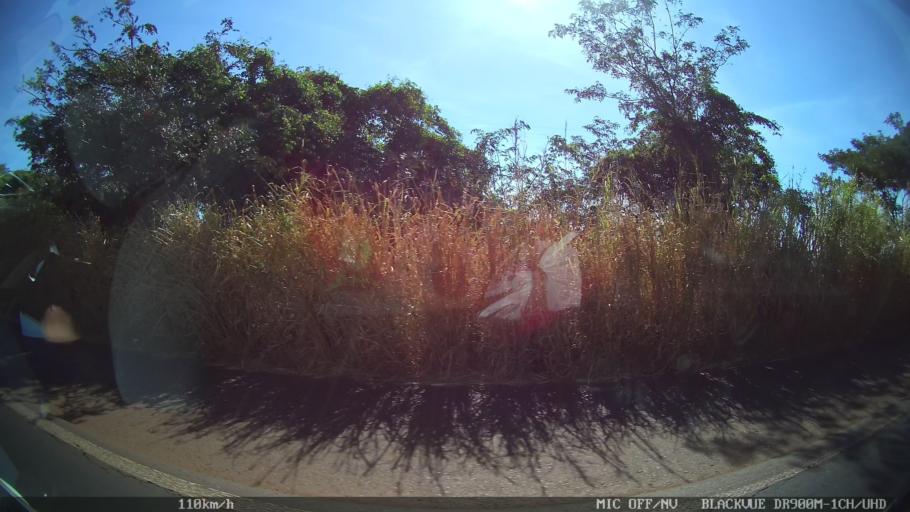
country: BR
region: Sao Paulo
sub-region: Barretos
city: Barretos
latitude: -20.4805
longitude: -48.5033
